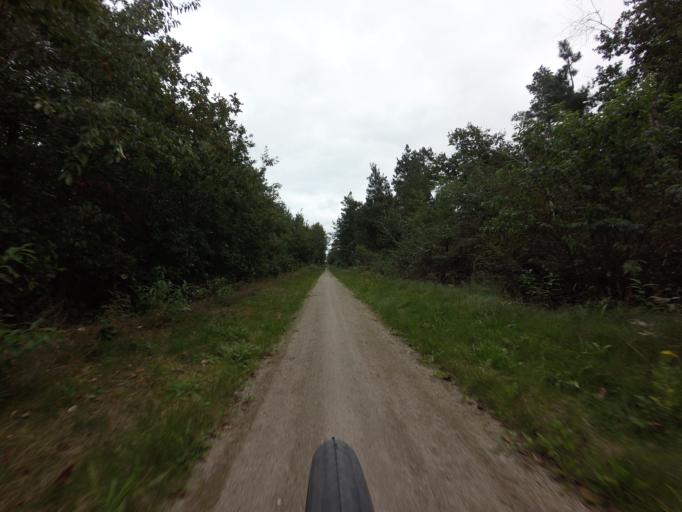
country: DK
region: South Denmark
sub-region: Billund Kommune
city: Grindsted
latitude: 55.8007
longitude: 9.0054
